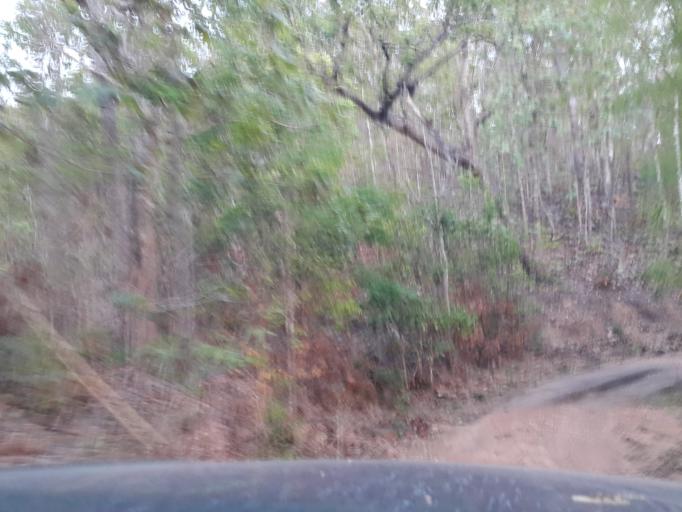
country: TH
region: Lamphun
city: Thung Hua Chang
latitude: 17.9040
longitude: 99.0811
